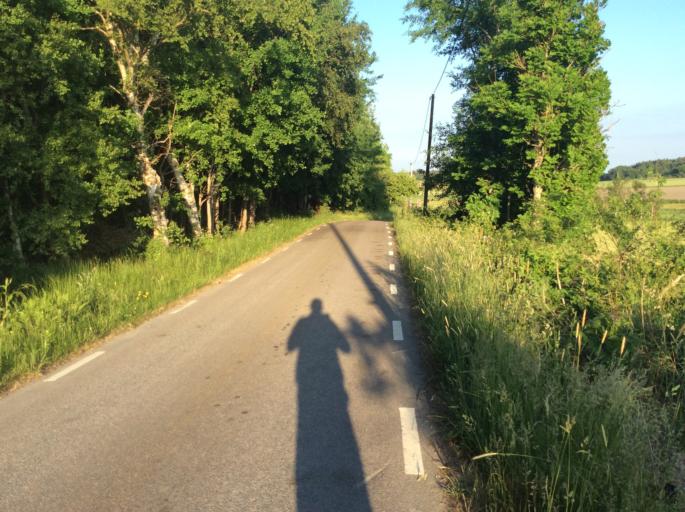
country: SE
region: Vaestra Goetaland
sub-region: Goteborg
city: Majorna
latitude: 57.7921
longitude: 11.8798
